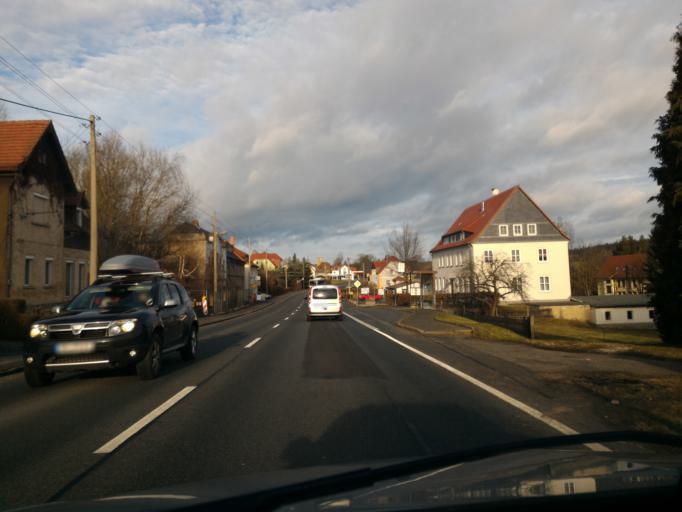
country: DE
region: Saxony
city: Friedersdorf
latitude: 51.0236
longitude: 14.5609
